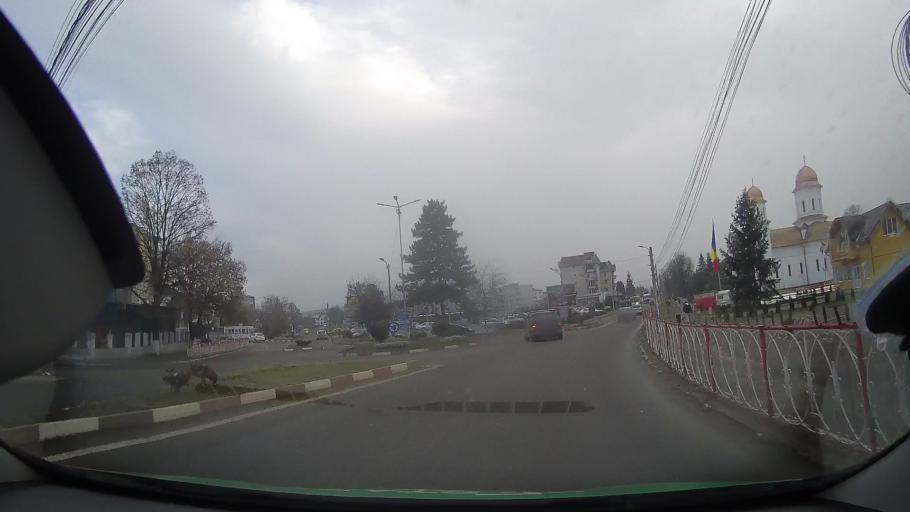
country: RO
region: Mures
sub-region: Municipiul Tarnaveni
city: Tarnaveni
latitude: 46.3318
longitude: 24.2949
